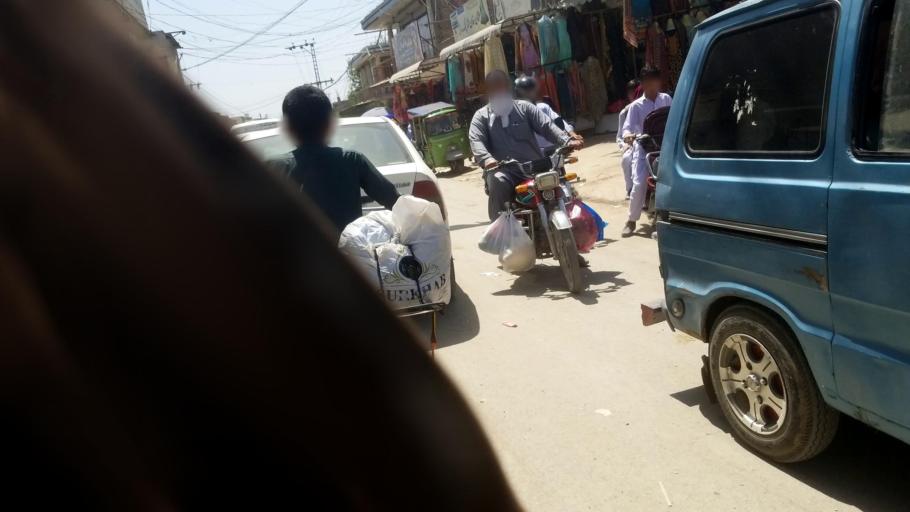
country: PK
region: Khyber Pakhtunkhwa
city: Peshawar
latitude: 34.0281
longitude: 71.4886
